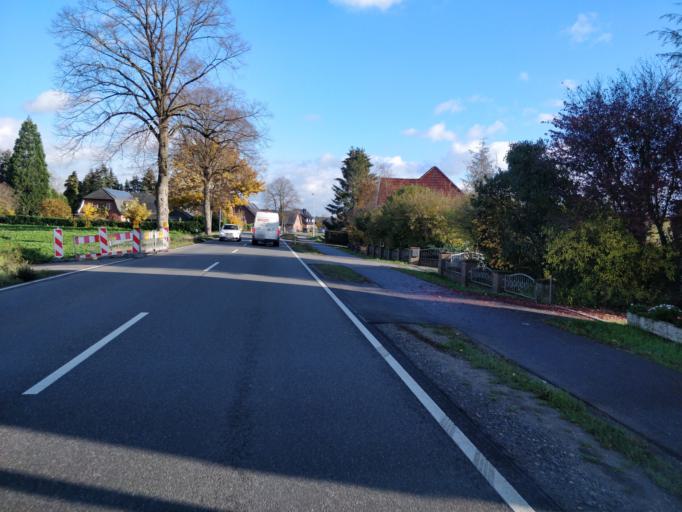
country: NL
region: Gelderland
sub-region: Oude IJsselstreek
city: Gendringen
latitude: 51.8242
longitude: 6.3286
